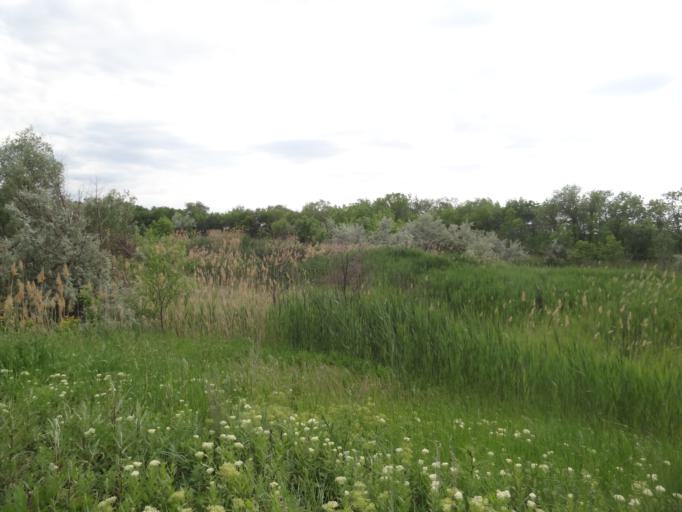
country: RU
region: Saratov
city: Engel's
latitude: 51.4333
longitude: 46.1304
